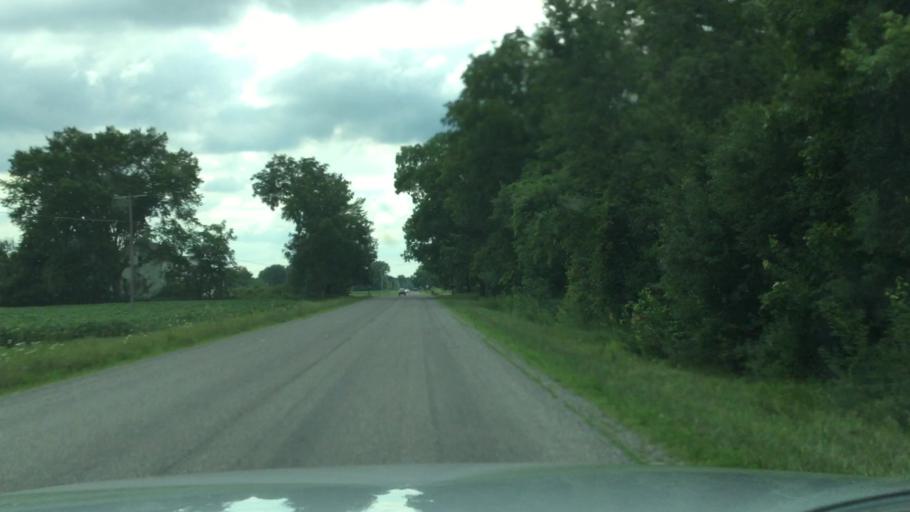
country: US
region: Michigan
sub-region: Saginaw County
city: Frankenmuth
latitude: 43.3218
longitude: -83.7843
